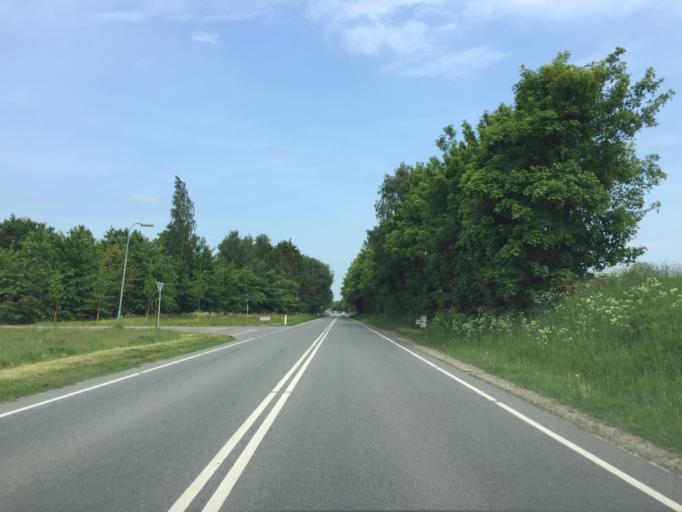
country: DK
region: South Denmark
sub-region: Nyborg Kommune
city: Nyborg
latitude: 55.1903
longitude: 10.7321
